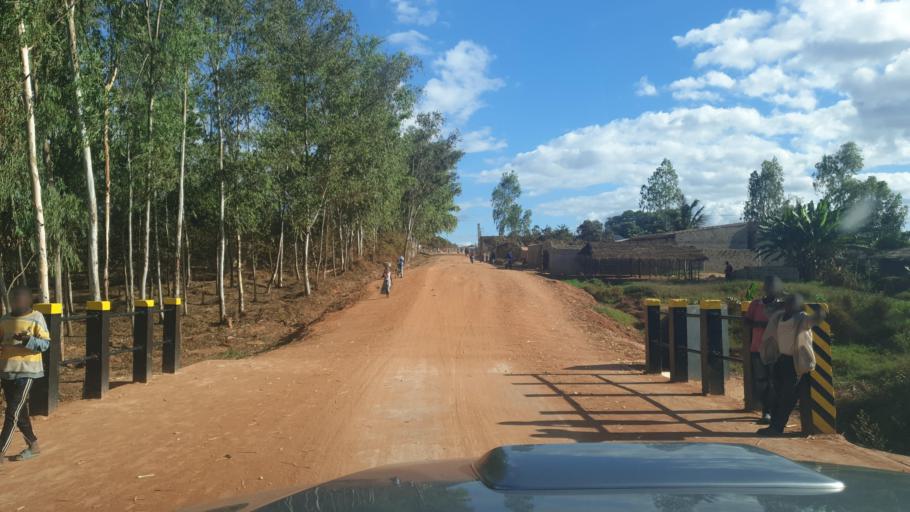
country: MZ
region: Nampula
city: Nampula
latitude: -15.0975
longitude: 39.2245
